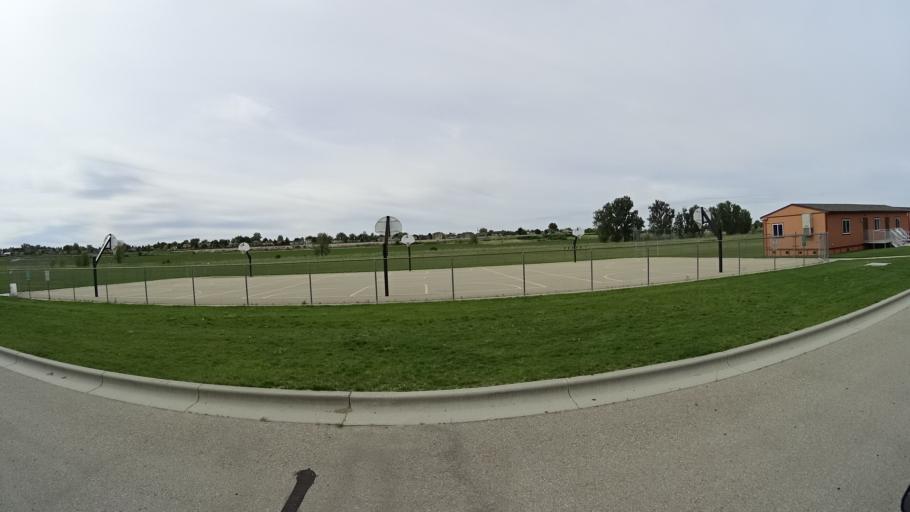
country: US
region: Idaho
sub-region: Ada County
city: Garden City
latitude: 43.5707
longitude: -116.2850
